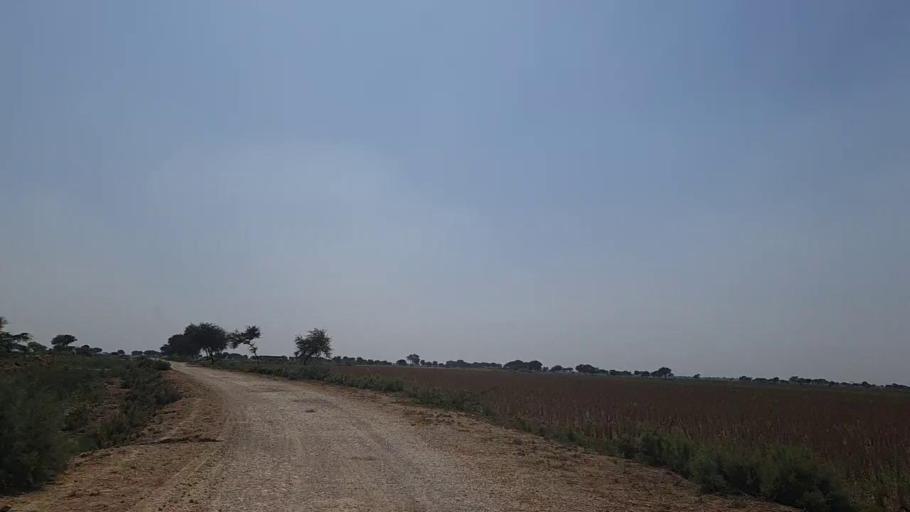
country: PK
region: Sindh
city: Jati
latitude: 24.5403
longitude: 68.3155
